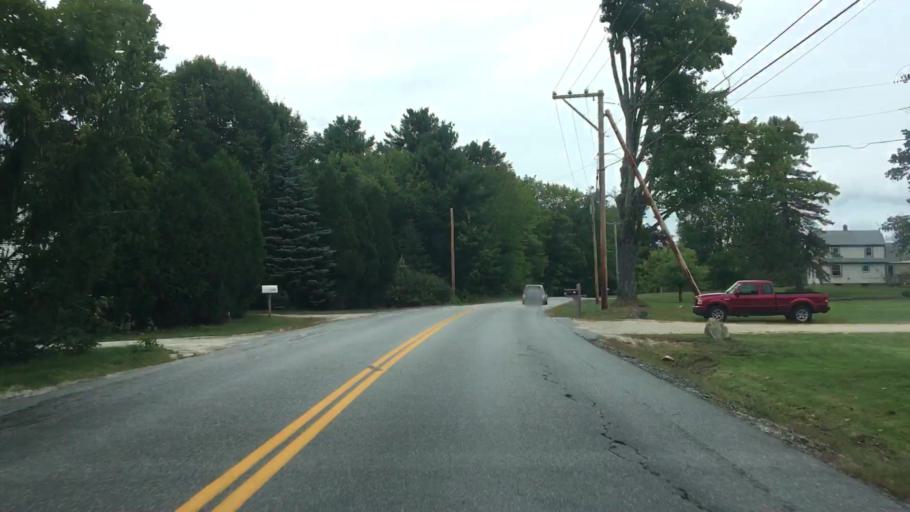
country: US
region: Maine
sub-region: Cumberland County
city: Yarmouth
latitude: 43.8464
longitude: -70.2139
